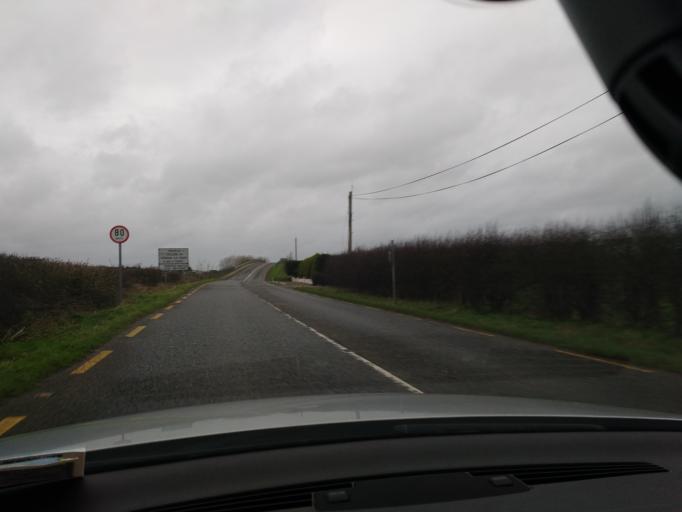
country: IE
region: Munster
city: Thurles
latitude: 52.6707
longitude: -7.6899
